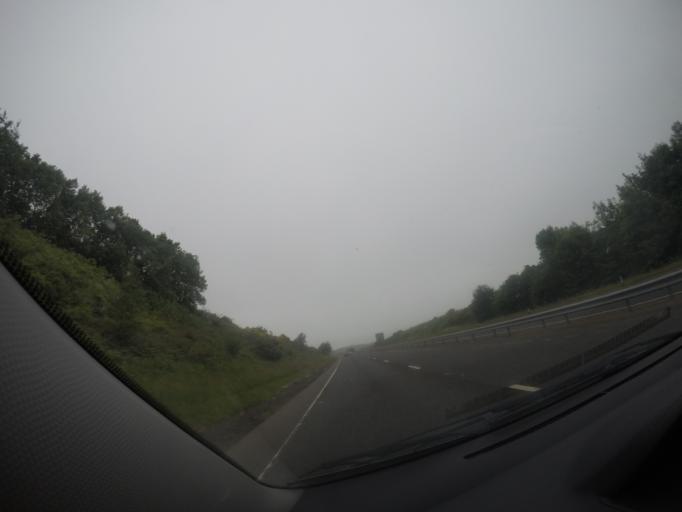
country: GB
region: Scotland
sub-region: Angus
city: Forfar
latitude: 56.6076
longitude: -2.9020
